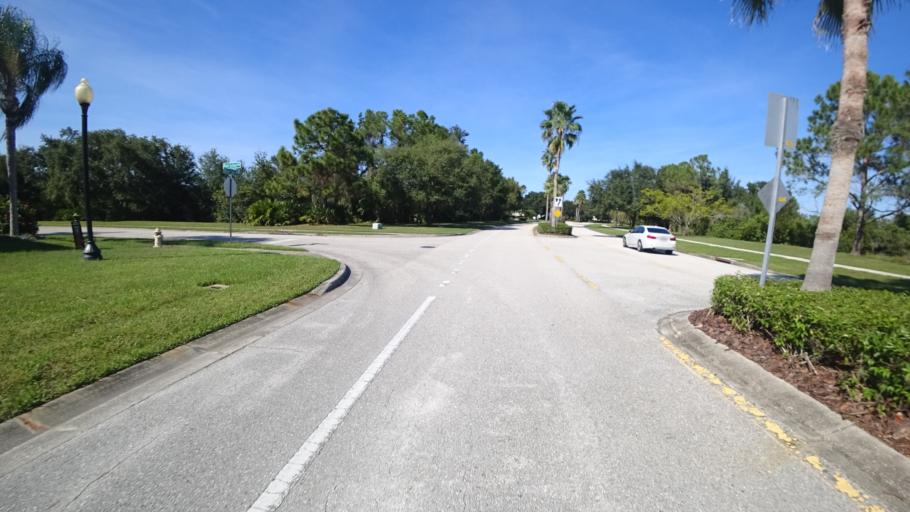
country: US
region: Florida
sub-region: Sarasota County
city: The Meadows
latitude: 27.4103
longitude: -82.4393
